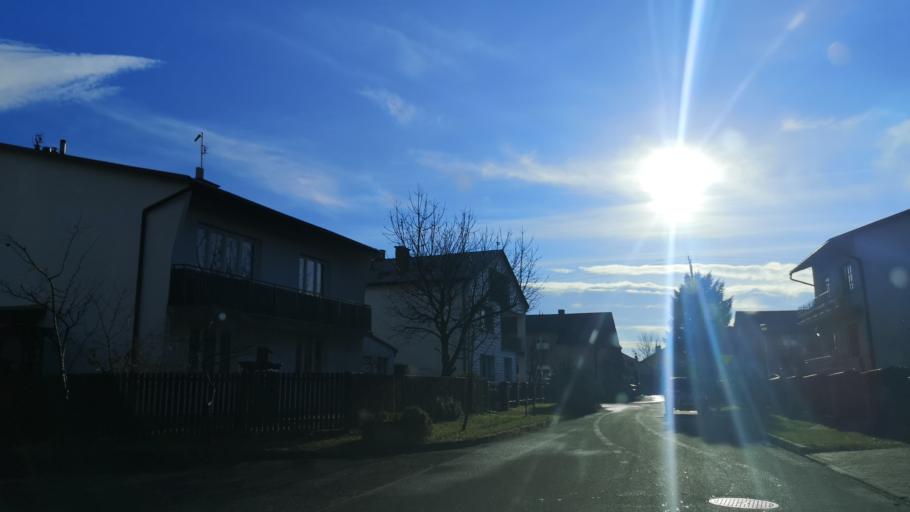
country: PL
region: Subcarpathian Voivodeship
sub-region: Powiat lezajski
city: Lezajsk
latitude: 50.2648
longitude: 22.4294
